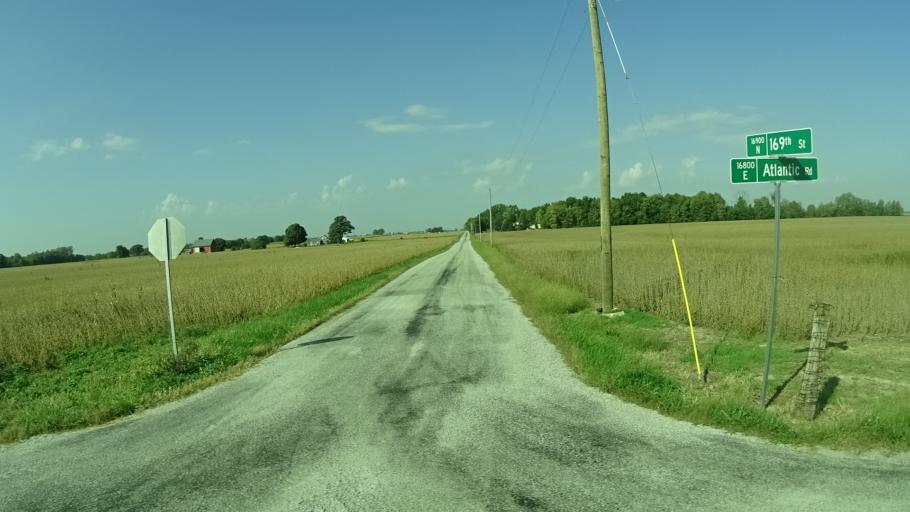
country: US
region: Indiana
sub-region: Madison County
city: Lapel
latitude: 40.0352
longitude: -85.8624
